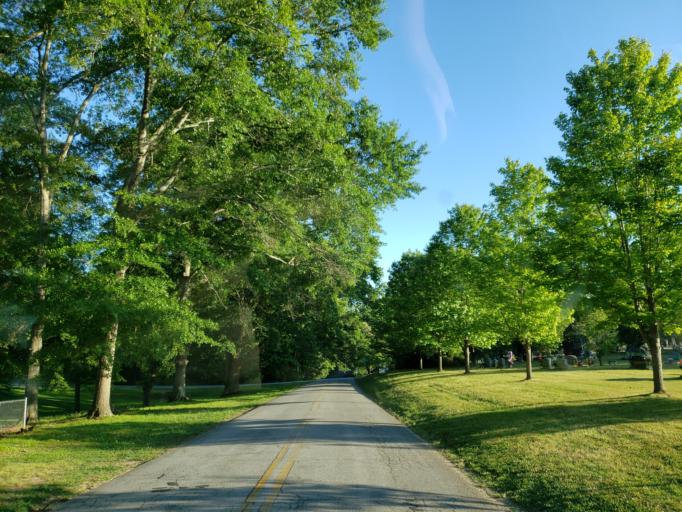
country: US
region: Georgia
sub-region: Haralson County
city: Tallapoosa
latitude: 33.7480
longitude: -85.2949
